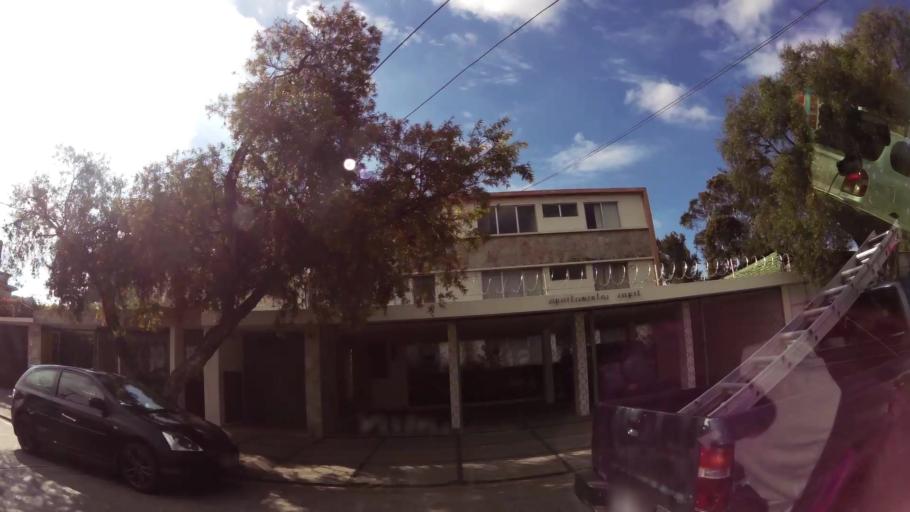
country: GT
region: Guatemala
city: Guatemala City
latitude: 14.6027
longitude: -90.5195
